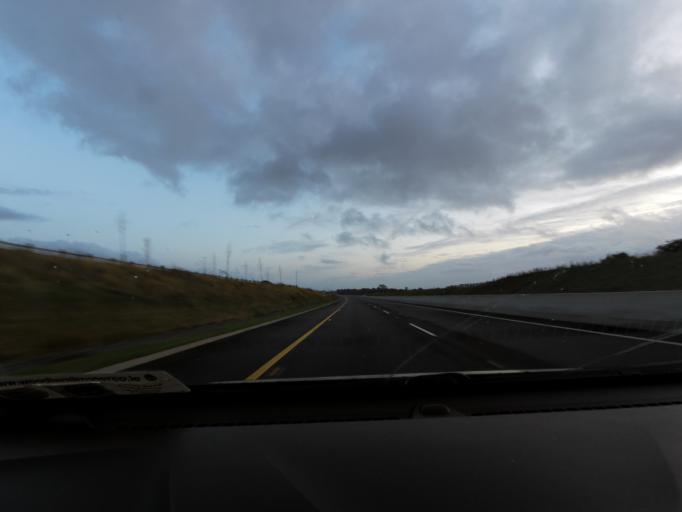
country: IE
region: Connaught
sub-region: County Galway
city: Athenry
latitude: 53.3287
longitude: -8.8032
